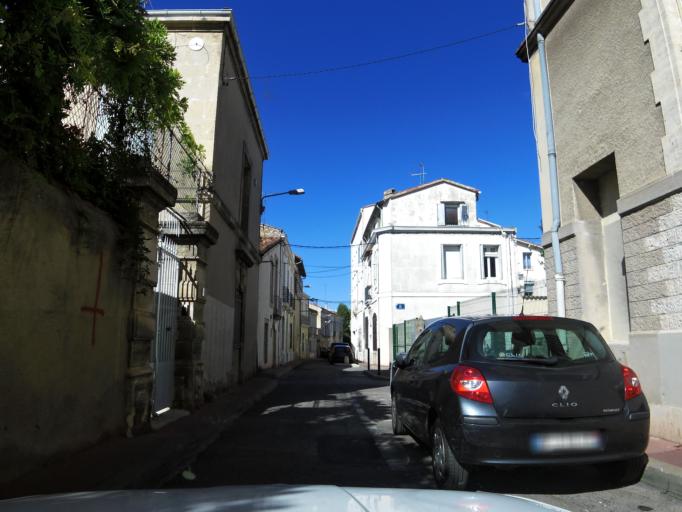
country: FR
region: Languedoc-Roussillon
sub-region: Departement de l'Herault
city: Montpellier
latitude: 43.6136
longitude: 3.8689
